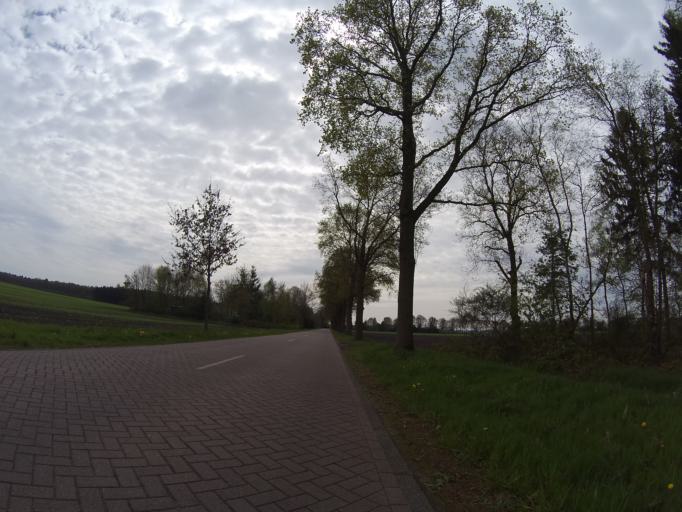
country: NL
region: Drenthe
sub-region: Gemeente Borger-Odoorn
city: Borger
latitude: 52.8756
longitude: 6.7827
